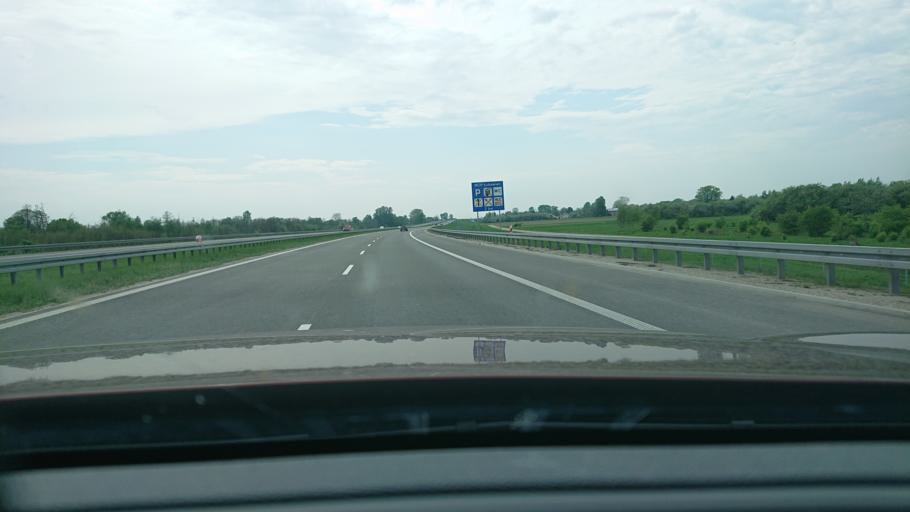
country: PL
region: Subcarpathian Voivodeship
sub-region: Powiat lancucki
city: Czarna
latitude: 50.0942
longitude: 22.2027
